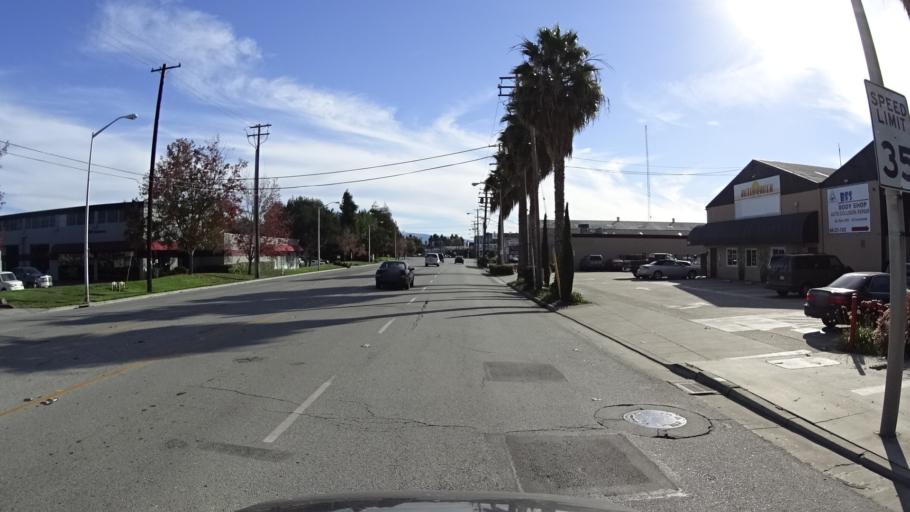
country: US
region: California
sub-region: Santa Clara County
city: Santa Clara
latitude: 37.3685
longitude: -121.9503
